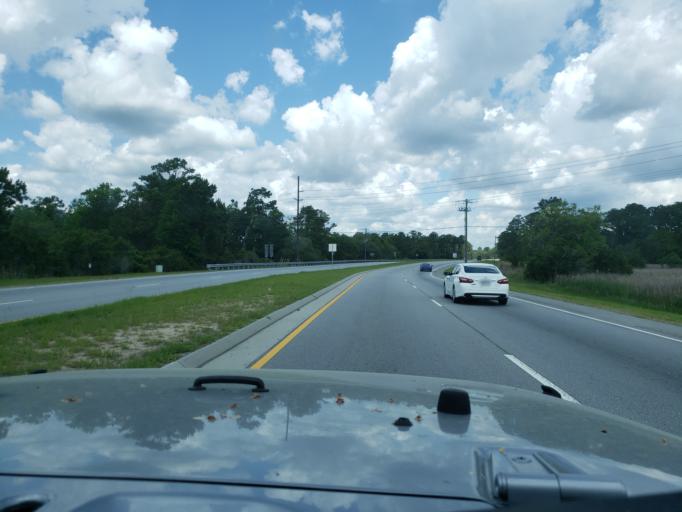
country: US
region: Georgia
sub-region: Chatham County
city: Georgetown
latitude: 32.0404
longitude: -81.2085
